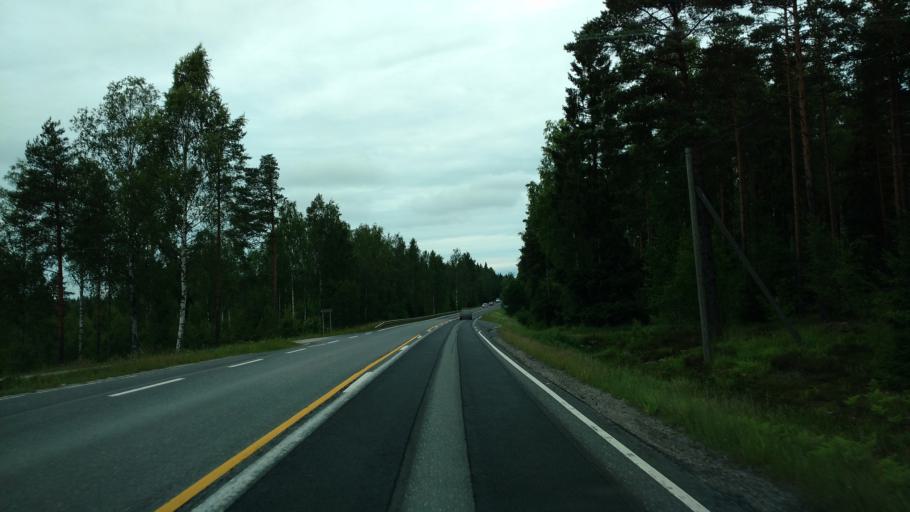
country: FI
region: Varsinais-Suomi
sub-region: Salo
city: Halikko
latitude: 60.4538
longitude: 23.0260
